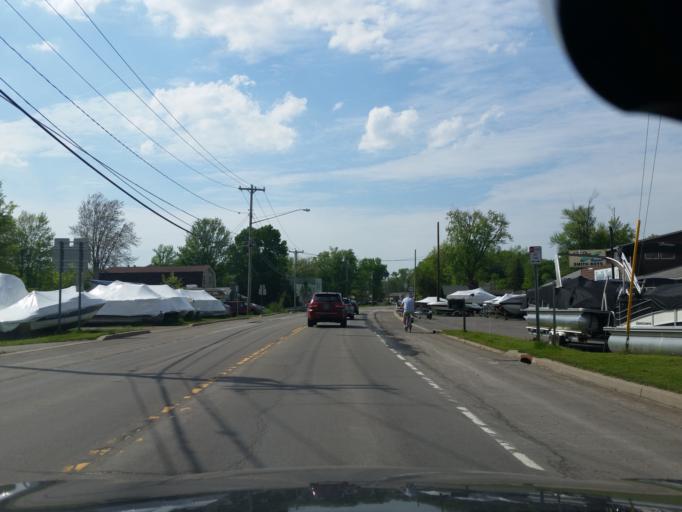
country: US
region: New York
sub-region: Chautauqua County
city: Lakewood
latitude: 42.1003
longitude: -79.3554
